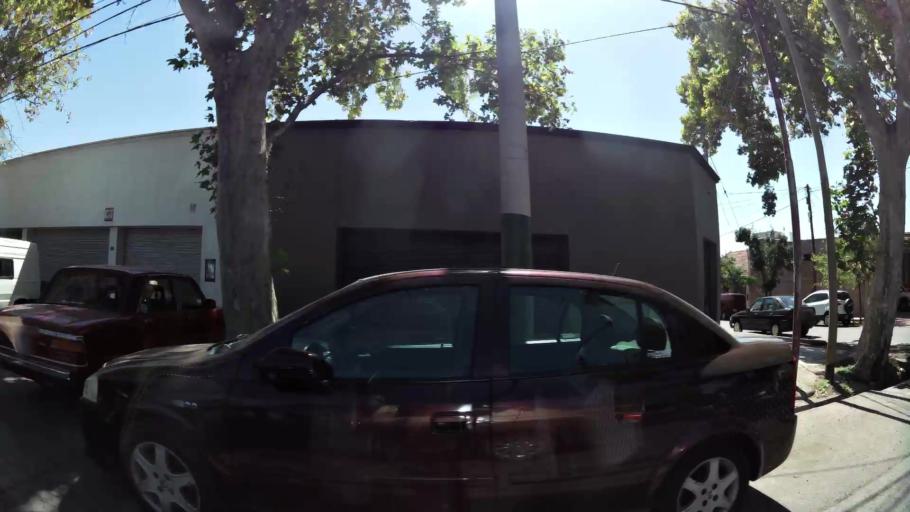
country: AR
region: Mendoza
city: Mendoza
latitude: -32.8950
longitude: -68.8157
